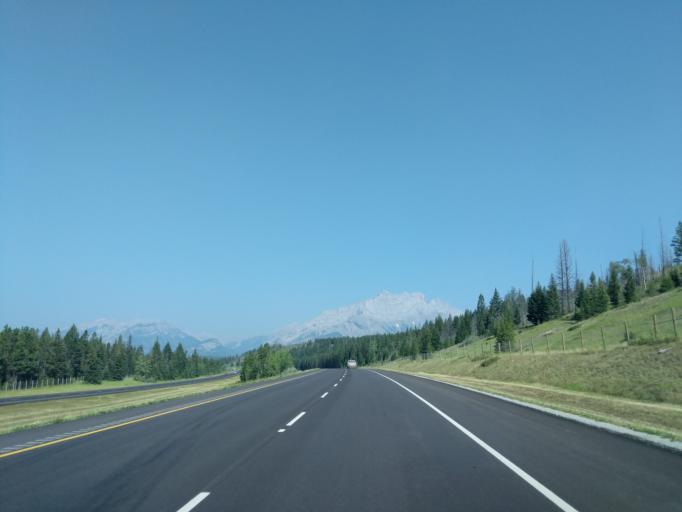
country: CA
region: Alberta
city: Canmore
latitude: 51.1641
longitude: -115.4444
